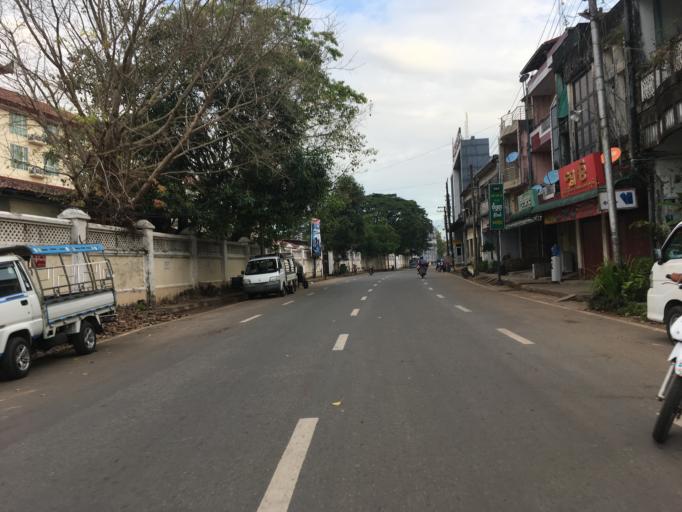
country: MM
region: Mon
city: Mawlamyine
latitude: 16.4965
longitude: 97.6190
